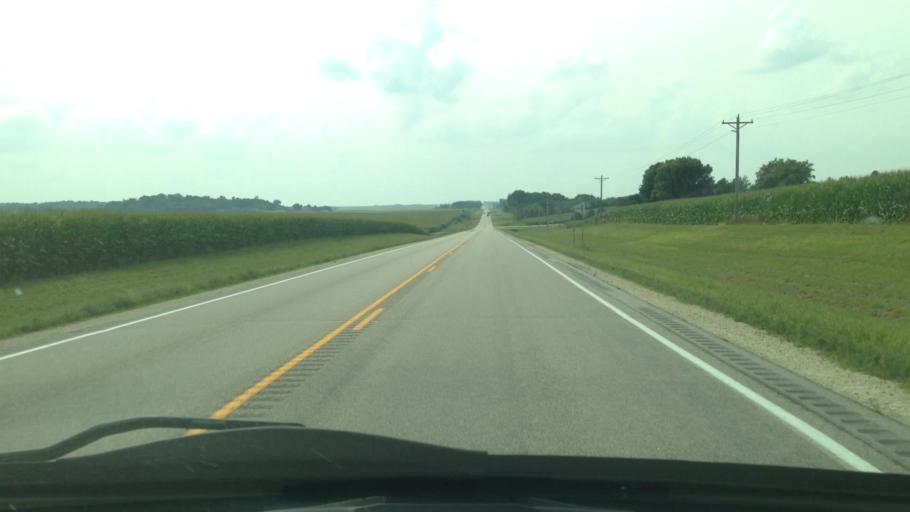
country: US
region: Minnesota
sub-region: Wabasha County
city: Elgin
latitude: 44.1654
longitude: -92.2640
